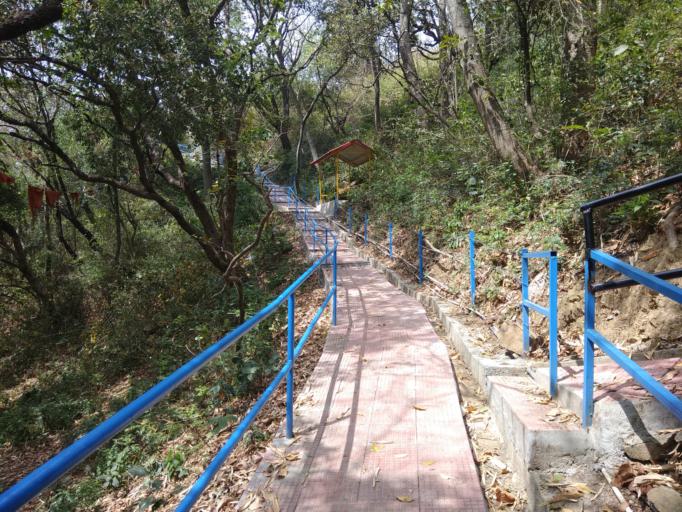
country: IN
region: Himachal Pradesh
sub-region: Kangra
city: Palampur
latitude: 32.0761
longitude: 76.6244
